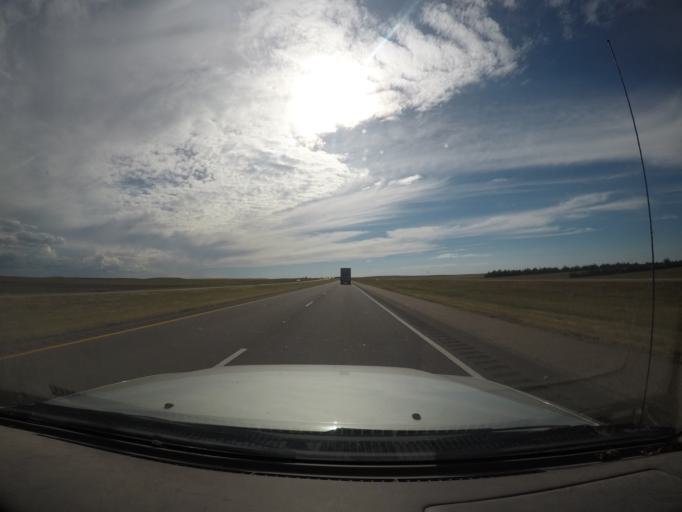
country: US
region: Nebraska
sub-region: Kimball County
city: Kimball
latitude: 41.1922
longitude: -103.8329
